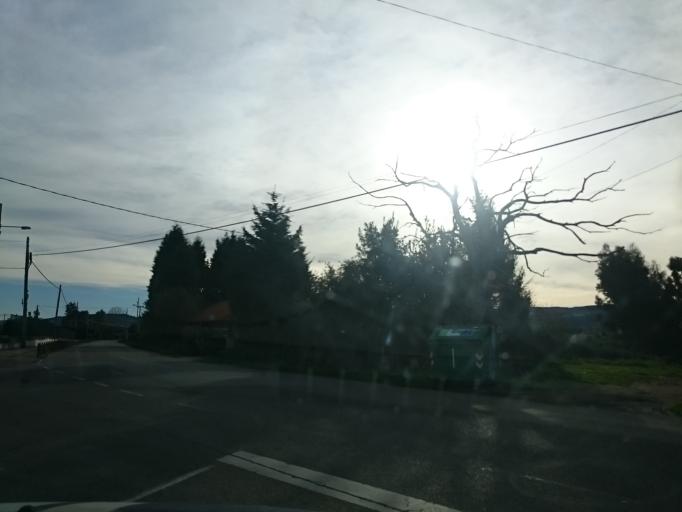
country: ES
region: Asturias
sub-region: Province of Asturias
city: Gijon
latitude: 43.5133
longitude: -5.6041
